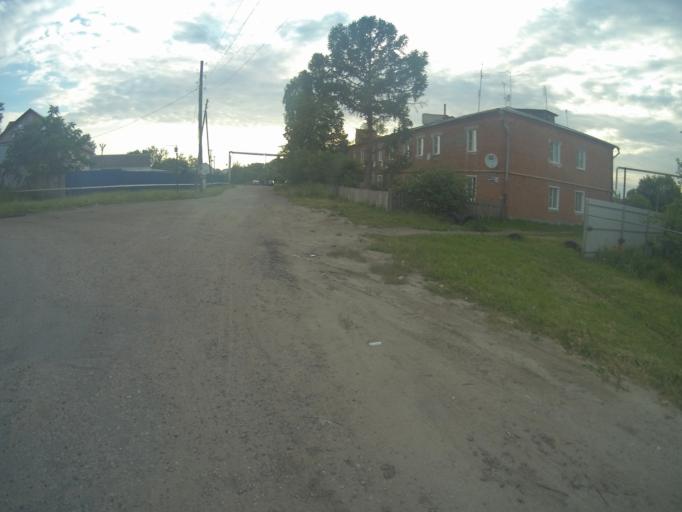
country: RU
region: Vladimir
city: Vladimir
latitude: 56.1941
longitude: 40.3864
